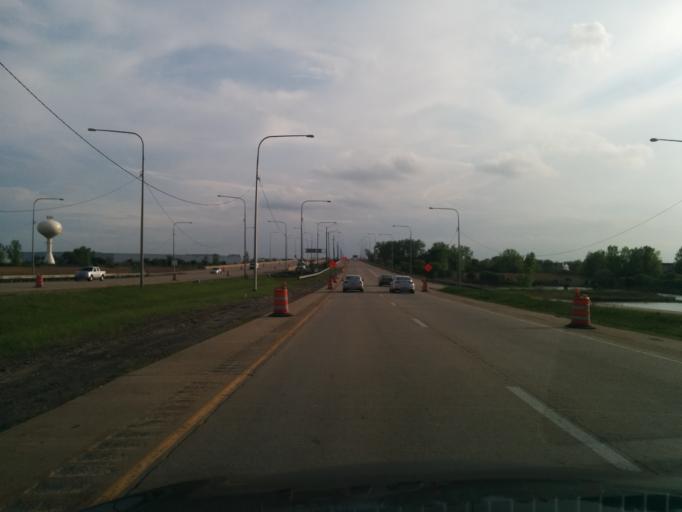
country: US
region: Illinois
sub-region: DuPage County
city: Hanover Park
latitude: 41.9930
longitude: -88.1225
